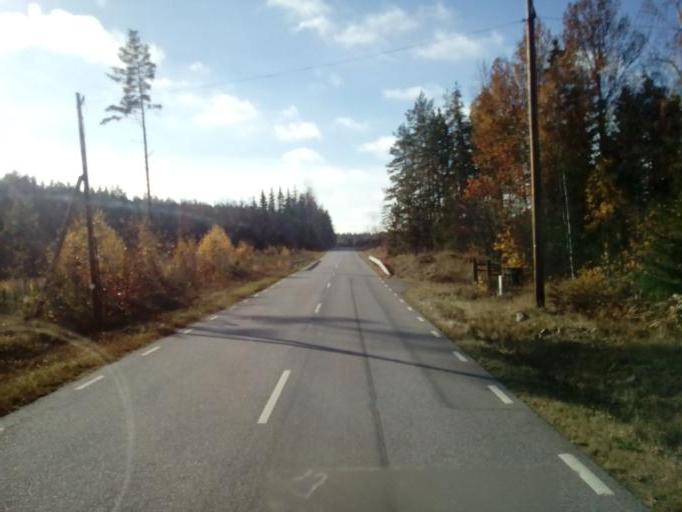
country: SE
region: Kalmar
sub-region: Vasterviks Kommun
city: Ankarsrum
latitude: 57.7460
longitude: 16.1120
